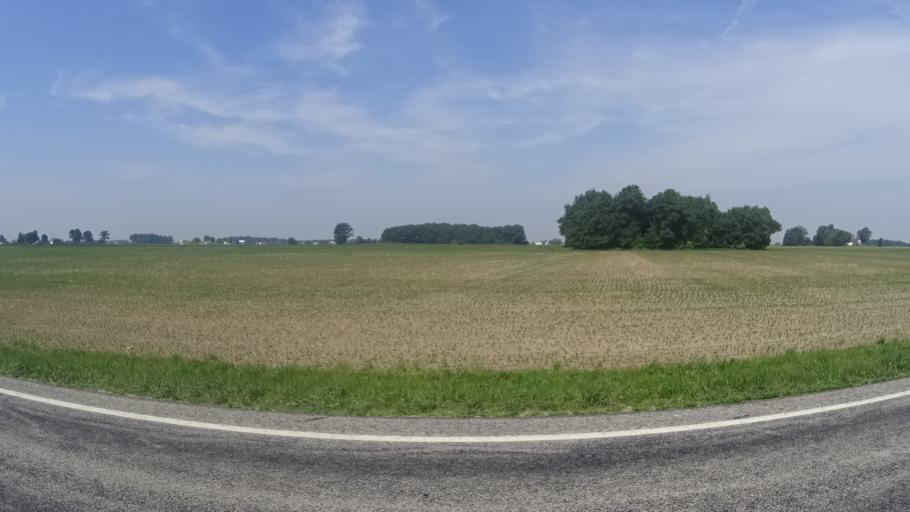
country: US
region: Ohio
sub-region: Huron County
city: Monroeville
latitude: 41.3310
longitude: -82.7202
